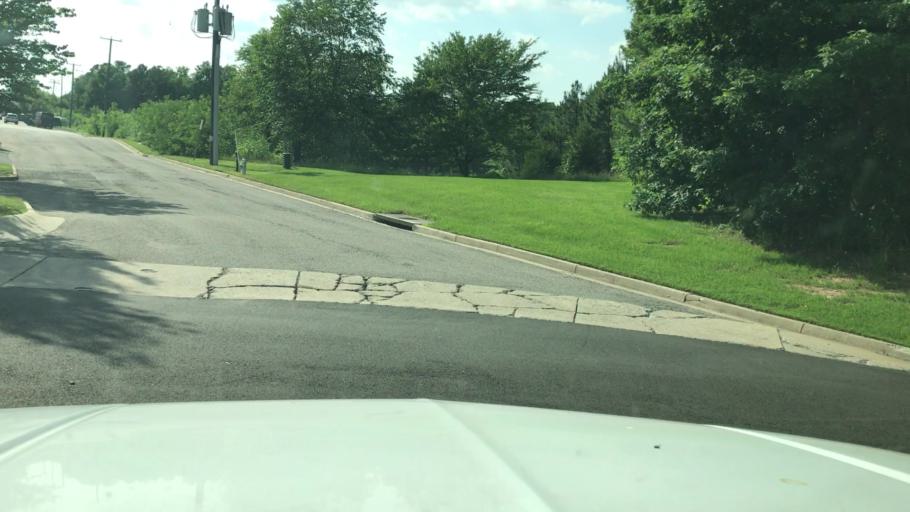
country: US
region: Virginia
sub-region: Henrico County
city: Short Pump
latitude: 37.6520
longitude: -77.6012
